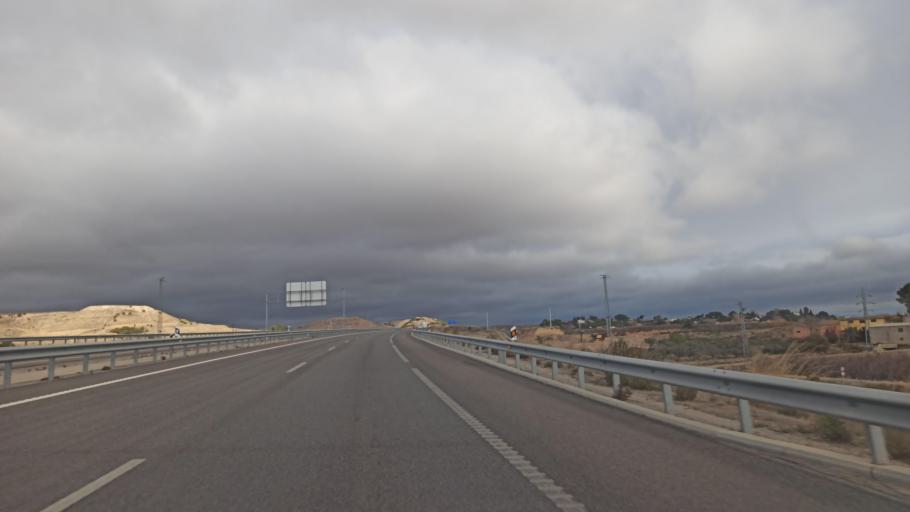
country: ES
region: Catalonia
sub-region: Provincia de Lleida
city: Alpicat
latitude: 41.6638
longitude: 0.5809
